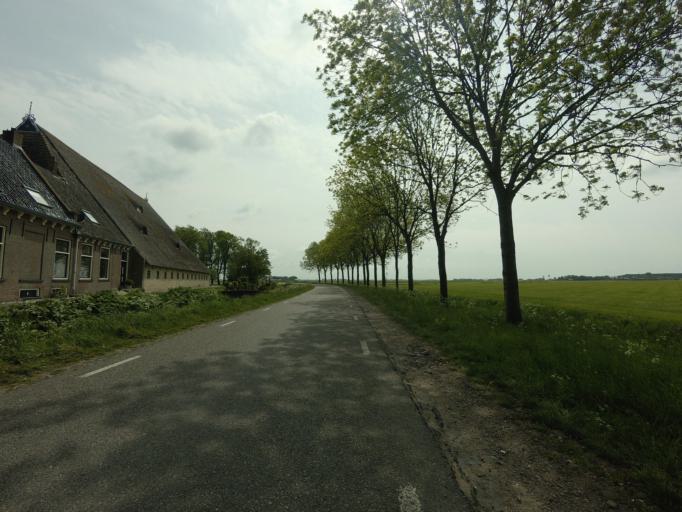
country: NL
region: Friesland
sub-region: Sudwest Fryslan
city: Bolsward
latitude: 53.1096
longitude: 5.4916
